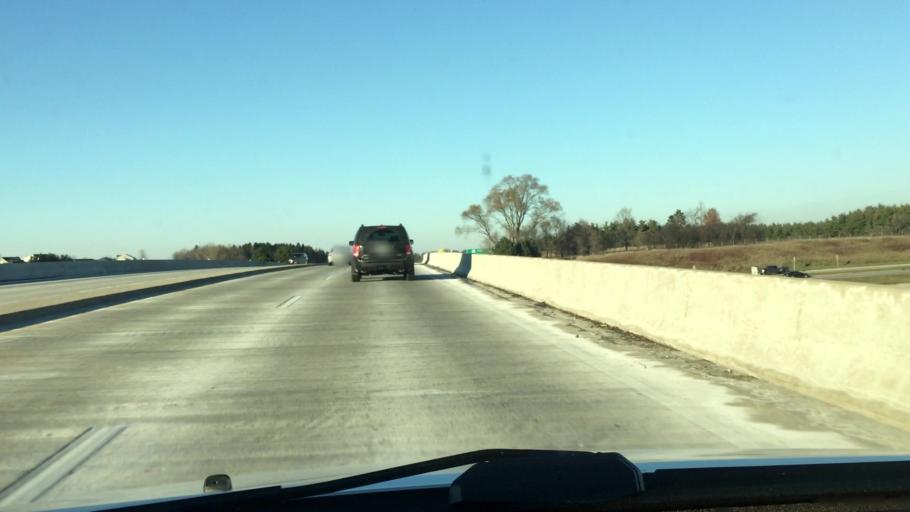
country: US
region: Wisconsin
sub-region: Waukesha County
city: Oconomowoc
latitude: 43.1057
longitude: -88.4803
